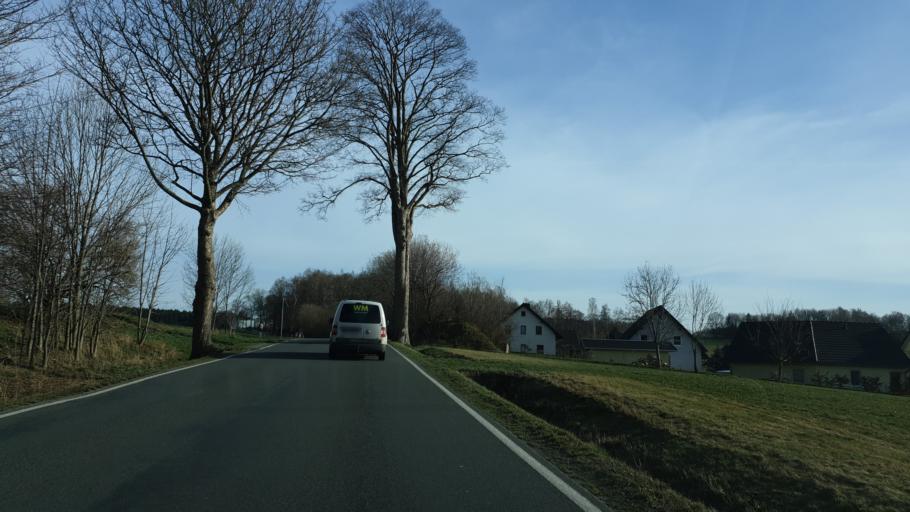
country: DE
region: Saxony
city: Zwonitz
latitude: 50.6528
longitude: 12.7746
